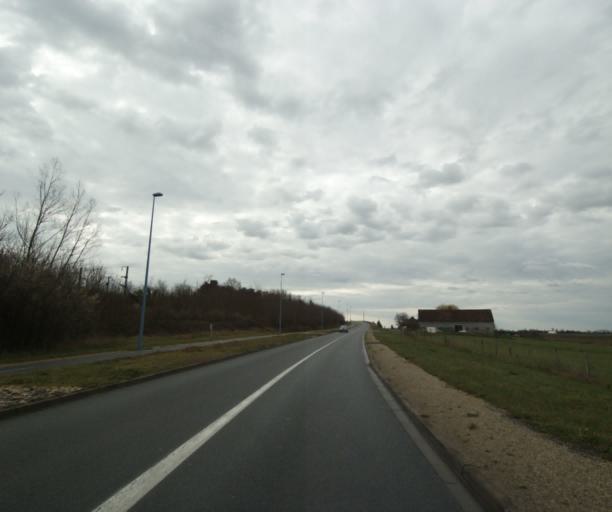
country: FR
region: Auvergne
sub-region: Departement de l'Allier
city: Toulon-sur-Allier
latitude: 46.5246
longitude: 3.3536
